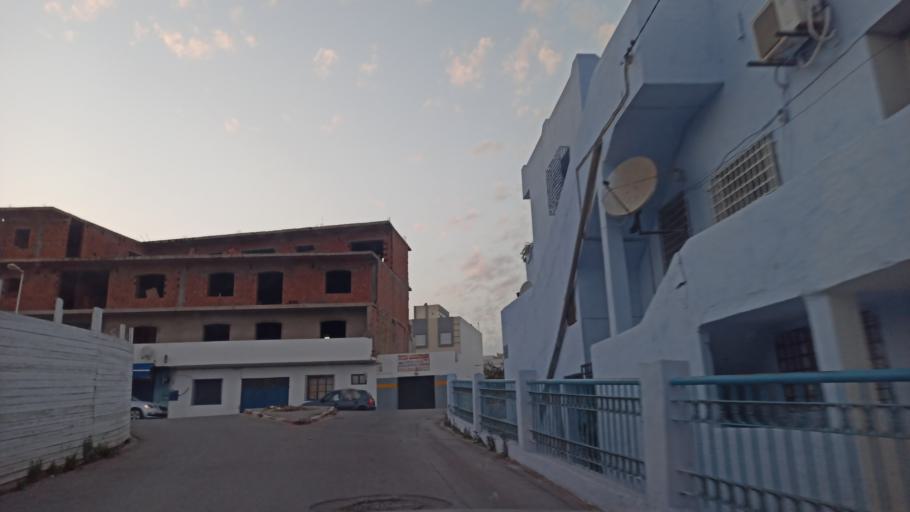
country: TN
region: Nabul
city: Al Hammamat
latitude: 36.4061
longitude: 10.6193
